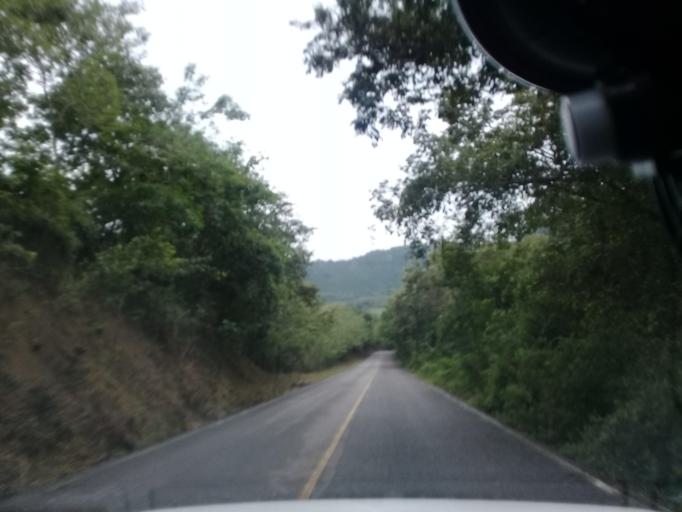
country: MX
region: Veracruz
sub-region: Chalma
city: San Pedro Coyutla
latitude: 21.2115
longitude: -98.4237
